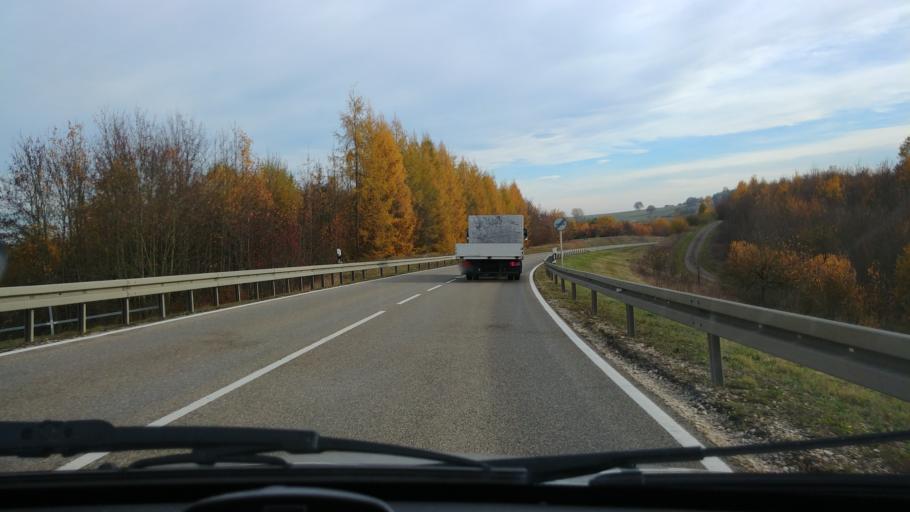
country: DE
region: Baden-Wuerttemberg
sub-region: Regierungsbezirk Stuttgart
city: Giengen an der Brenz
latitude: 48.6610
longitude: 10.2676
